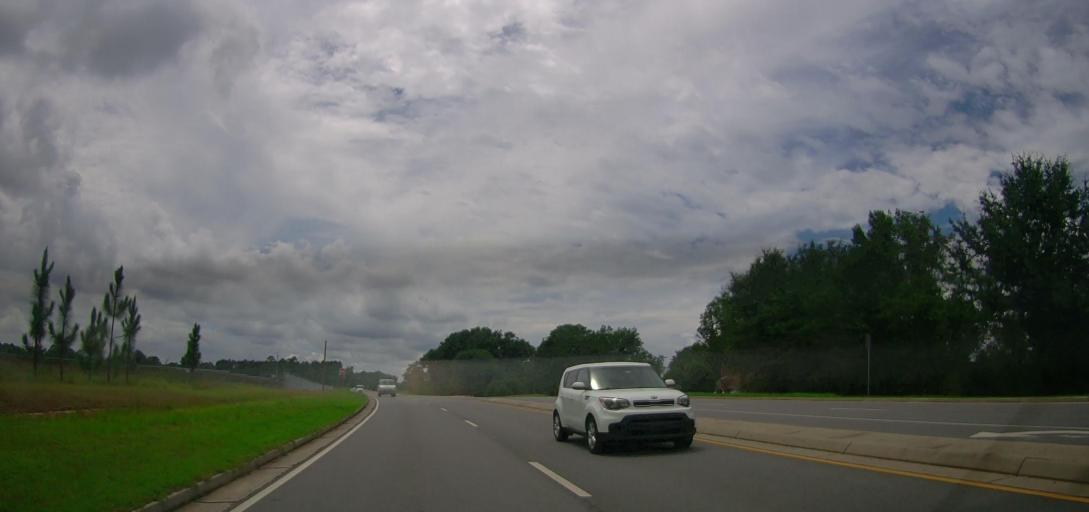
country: US
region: Georgia
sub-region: Telfair County
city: McRae
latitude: 32.0584
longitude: -82.8710
